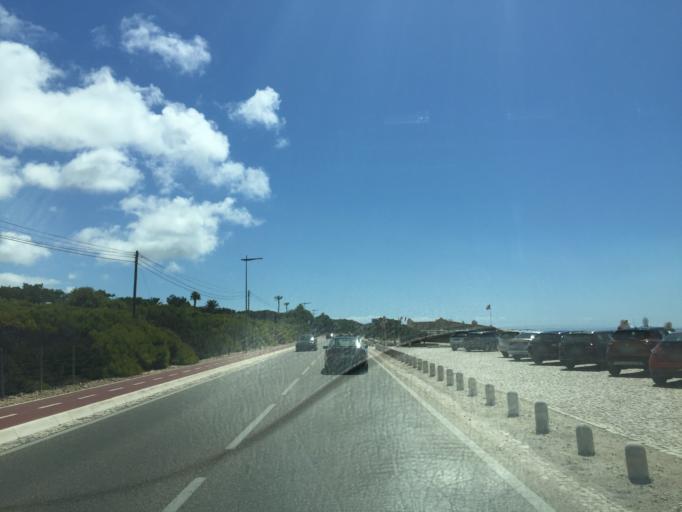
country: PT
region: Lisbon
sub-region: Cascais
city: Cascais
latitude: 38.7007
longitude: -9.4700
